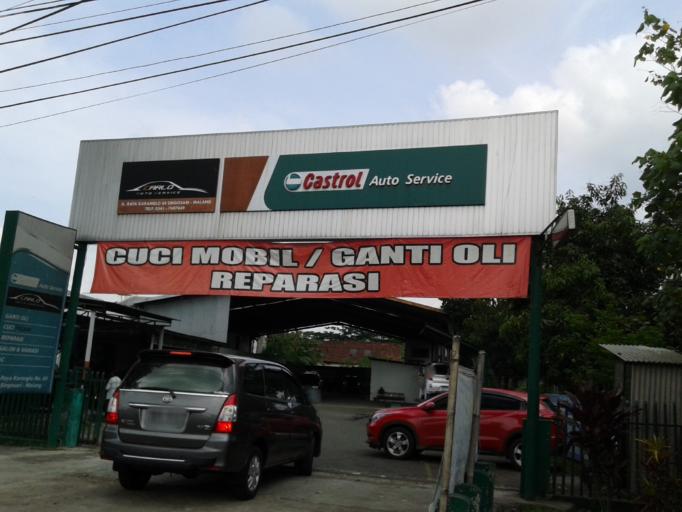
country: ID
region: East Java
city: Singosari
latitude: -7.9158
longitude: 112.6533
